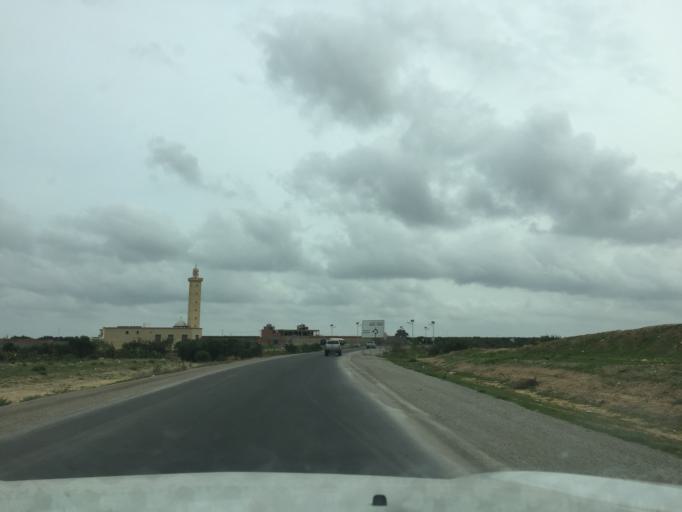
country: TN
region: Susah
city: Masakin
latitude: 35.6481
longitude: 10.5882
